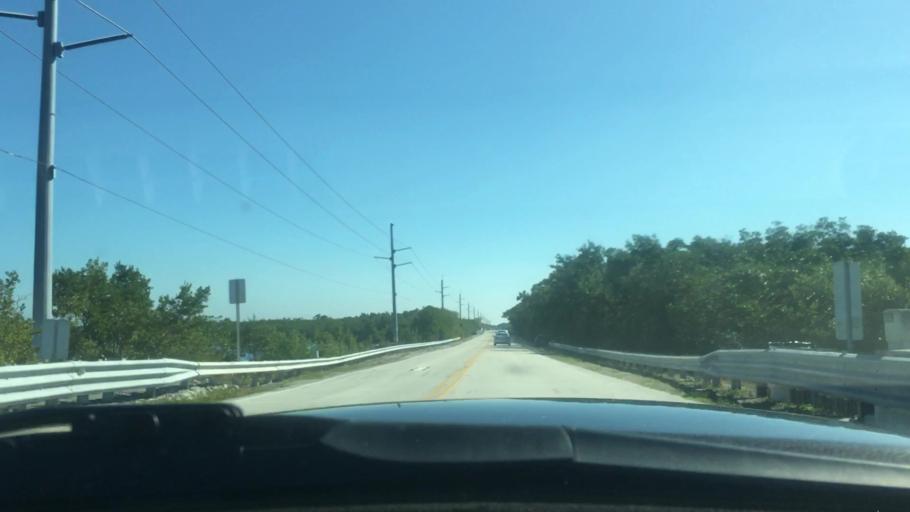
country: US
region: Florida
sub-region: Monroe County
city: North Key Largo
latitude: 25.2837
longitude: -80.3581
